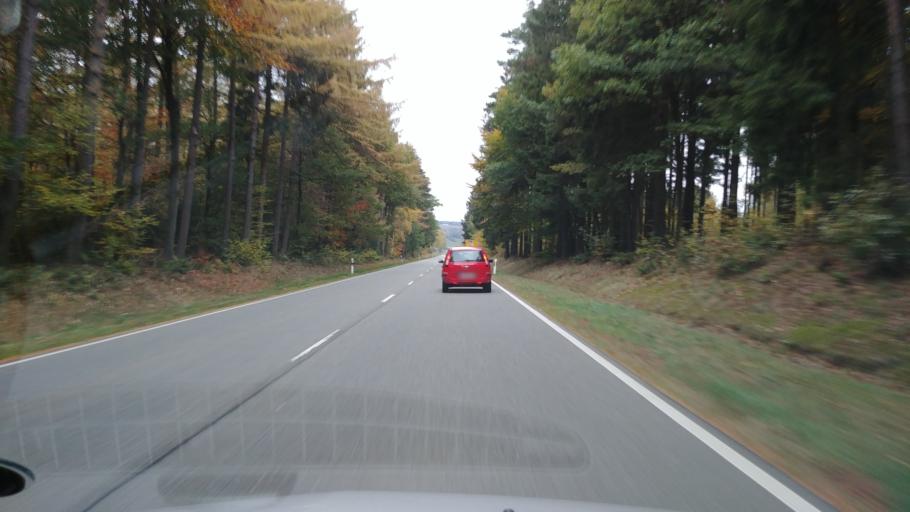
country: DE
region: Rheinland-Pfalz
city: Hilscheid
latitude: 49.7387
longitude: 7.0209
